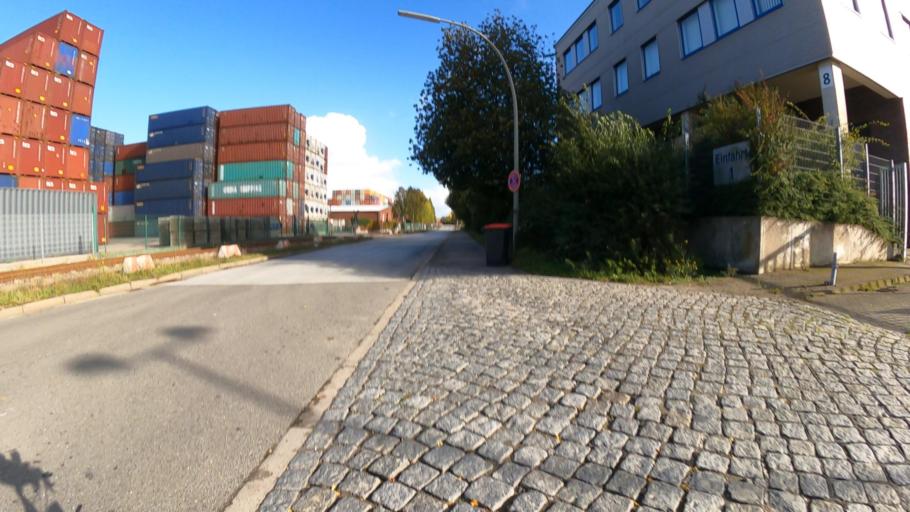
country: DE
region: Hamburg
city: Kleiner Grasbrook
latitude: 53.5133
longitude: 9.9606
